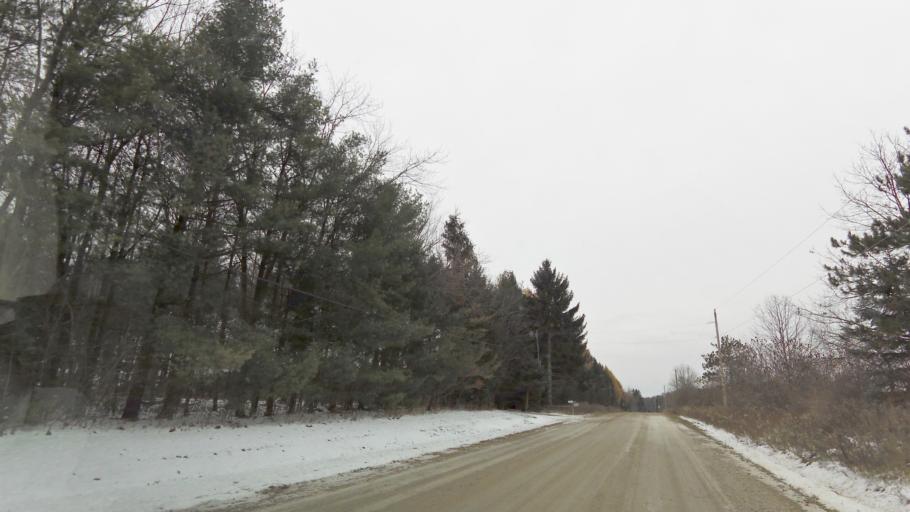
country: CA
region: Ontario
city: Vaughan
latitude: 43.9418
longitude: -79.6106
